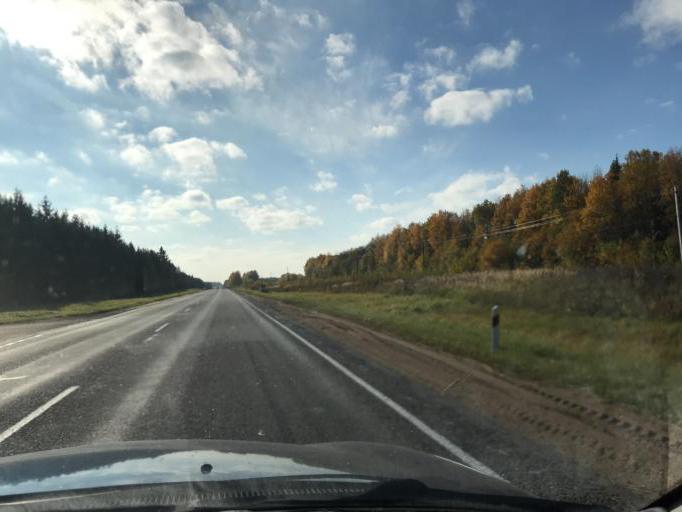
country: BY
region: Grodnenskaya
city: Voranava
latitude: 54.2142
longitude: 25.3527
